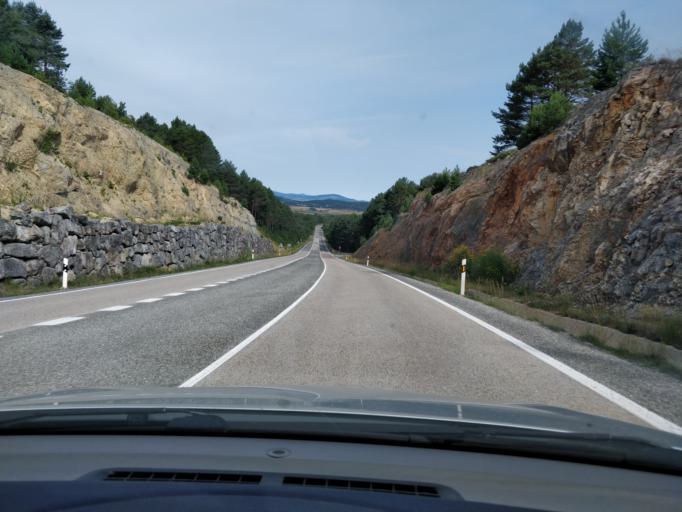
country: ES
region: Cantabria
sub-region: Provincia de Cantabria
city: San Martin de Elines
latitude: 42.9563
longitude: -3.7649
